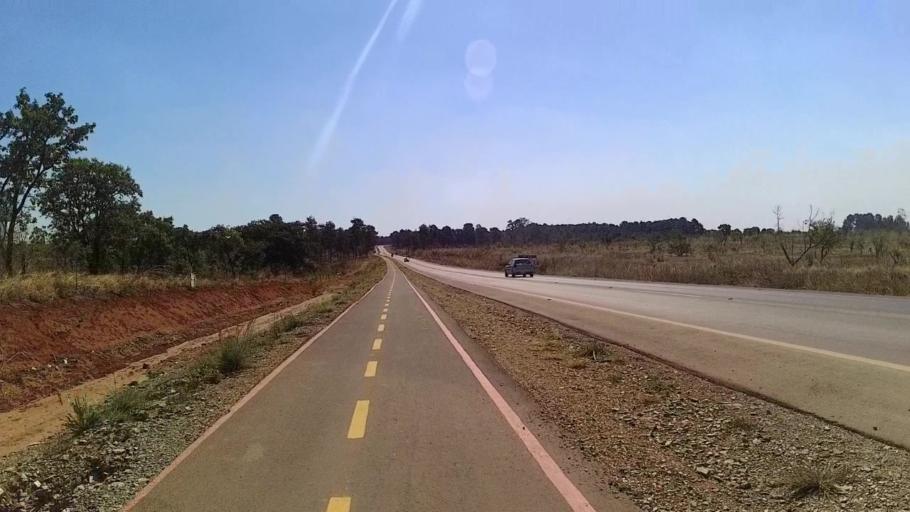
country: BR
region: Federal District
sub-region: Brasilia
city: Brasilia
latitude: -15.6793
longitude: -48.2346
